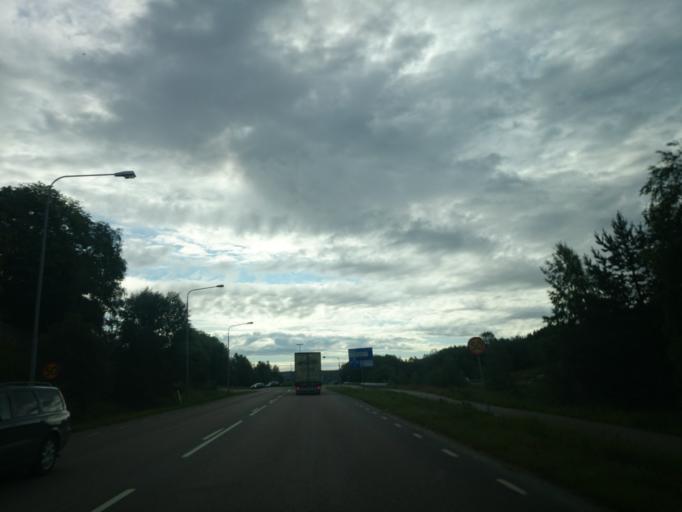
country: SE
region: Vaesternorrland
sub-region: Sundsvalls Kommun
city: Johannedal
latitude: 62.4130
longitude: 17.3655
